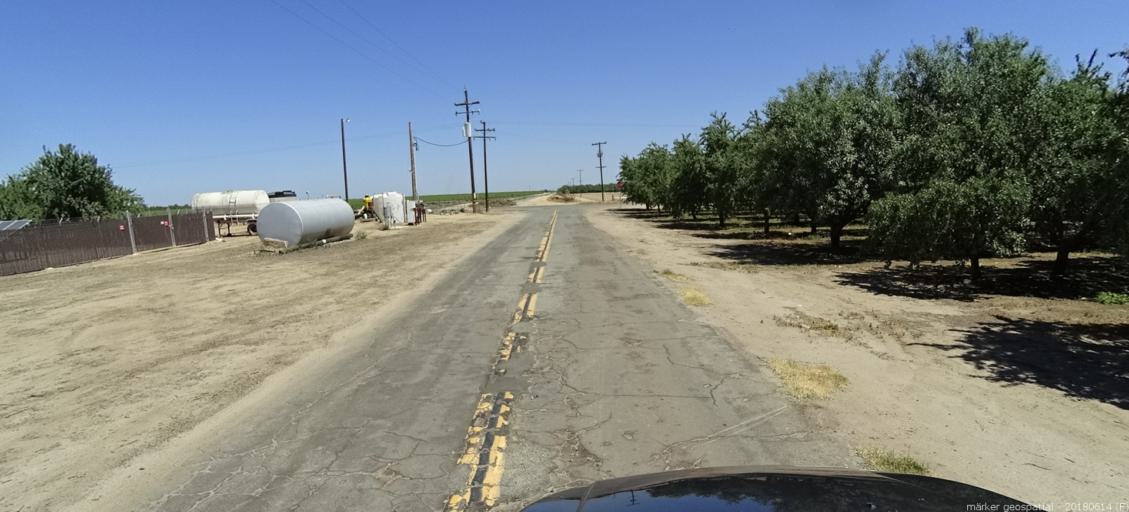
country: US
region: California
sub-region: Madera County
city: Fairmead
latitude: 37.0394
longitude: -120.2387
